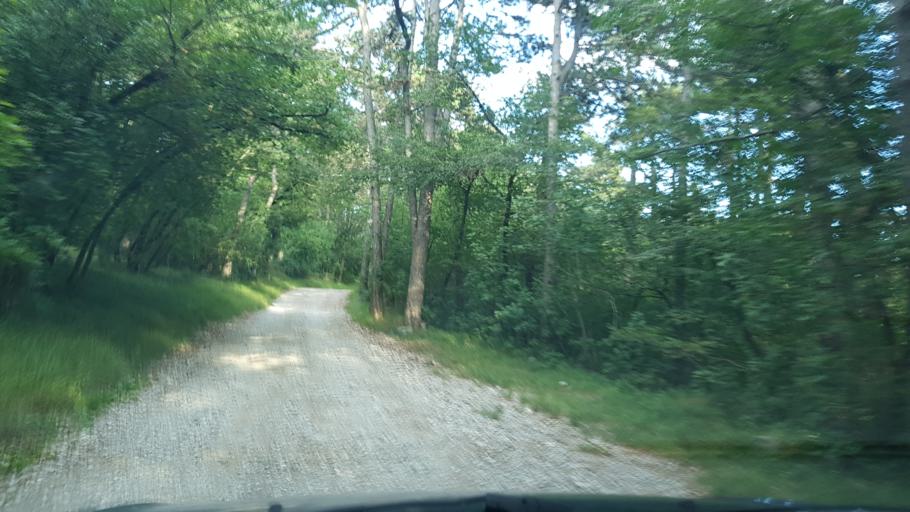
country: SI
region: Nova Gorica
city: Prvacina
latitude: 45.8559
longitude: 13.6985
